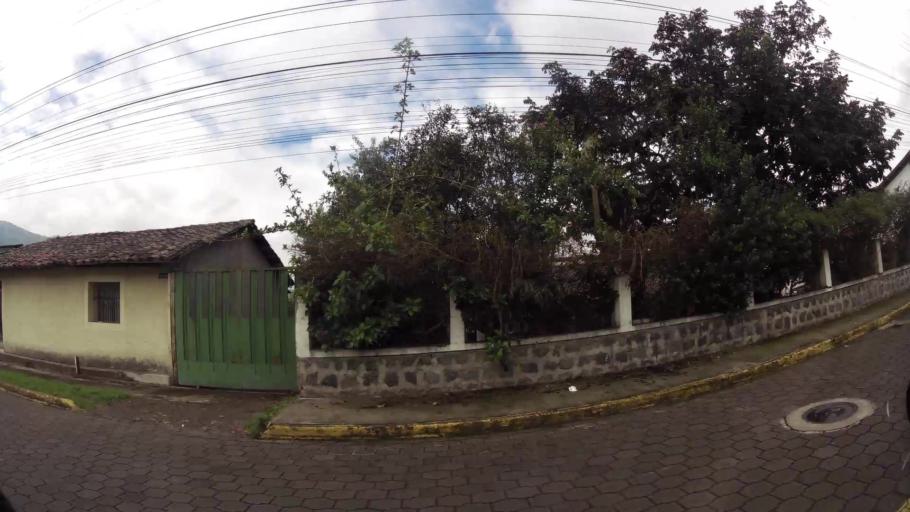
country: EC
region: Pichincha
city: Sangolqui
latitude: -0.3036
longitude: -78.4382
